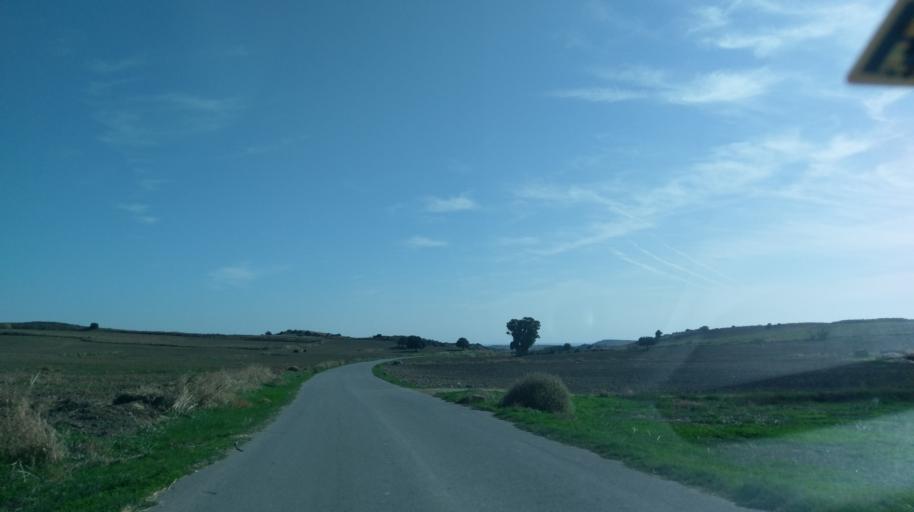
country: CY
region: Ammochostos
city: Trikomo
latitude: 35.3581
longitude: 33.9251
